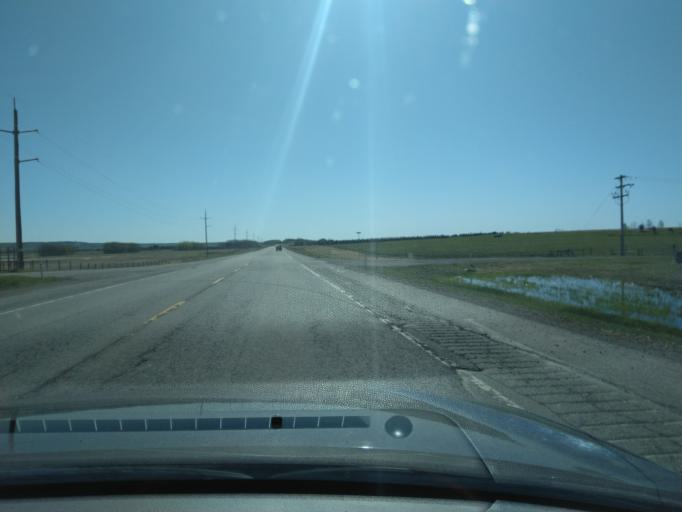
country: CA
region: Alberta
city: Cochrane
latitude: 51.0234
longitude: -114.3742
